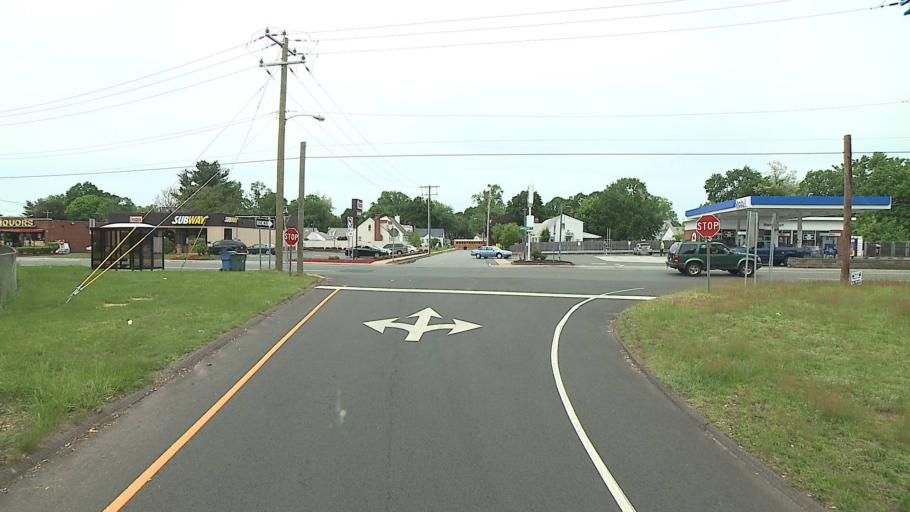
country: US
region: Connecticut
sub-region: Hartford County
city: Manchester
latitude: 41.7642
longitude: -72.5404
